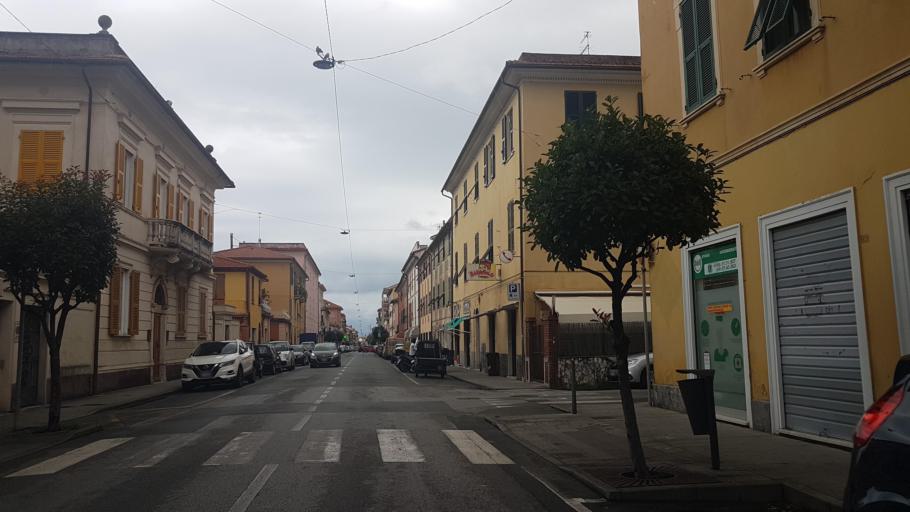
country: IT
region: Liguria
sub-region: Provincia di Genova
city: Sestri Levante
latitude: 44.2711
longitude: 9.4142
